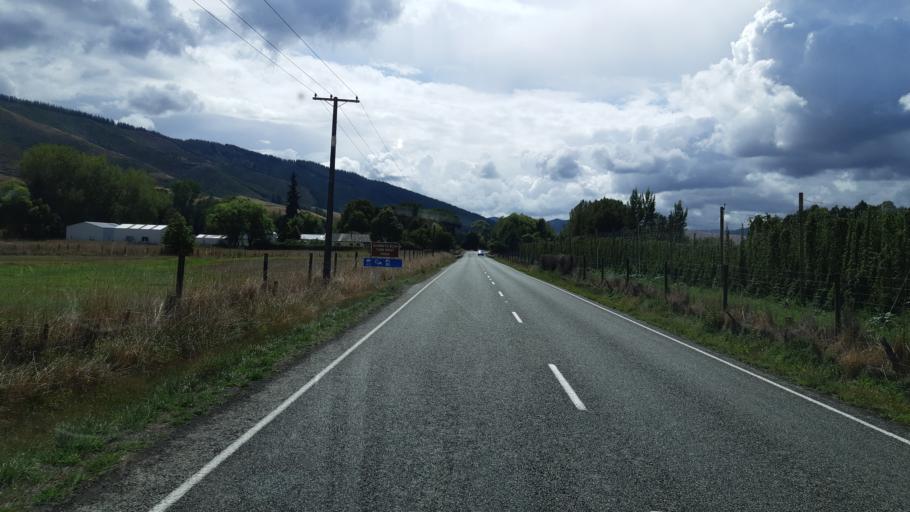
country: NZ
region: Tasman
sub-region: Tasman District
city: Wakefield
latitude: -41.4621
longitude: 172.8102
